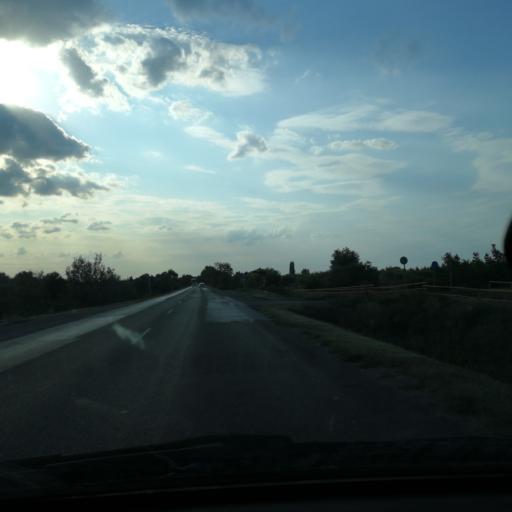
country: HU
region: Csongrad
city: Csongrad
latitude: 46.6849
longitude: 20.1799
